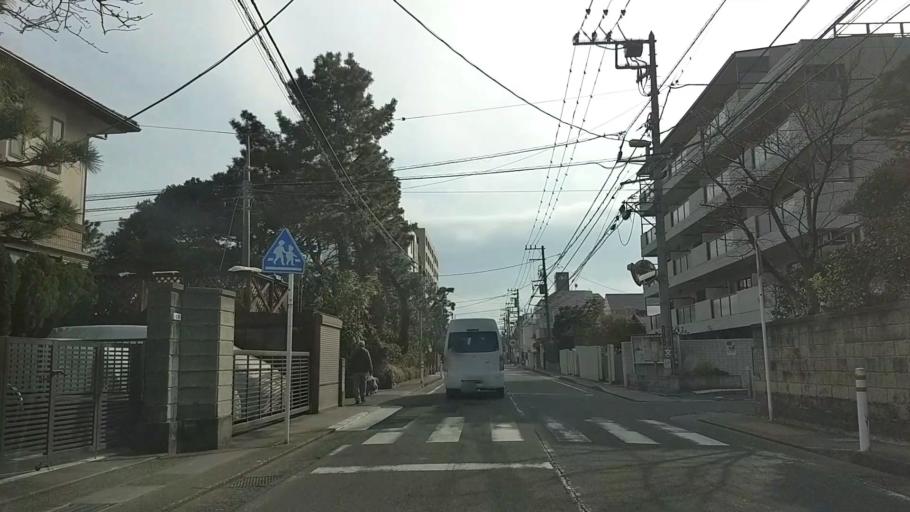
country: JP
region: Kanagawa
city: Chigasaki
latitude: 35.3215
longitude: 139.4082
